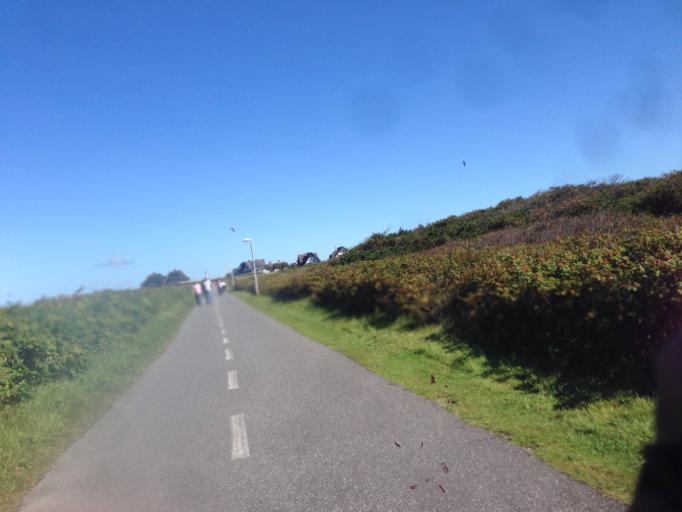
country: DE
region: Schleswig-Holstein
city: Westerland
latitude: 54.9273
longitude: 8.3111
